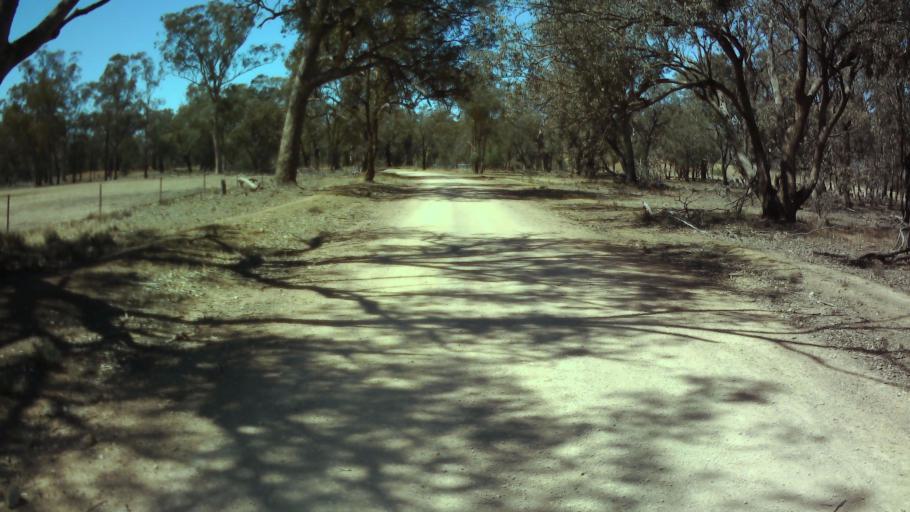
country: AU
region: New South Wales
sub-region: Weddin
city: Grenfell
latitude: -33.9364
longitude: 148.0775
